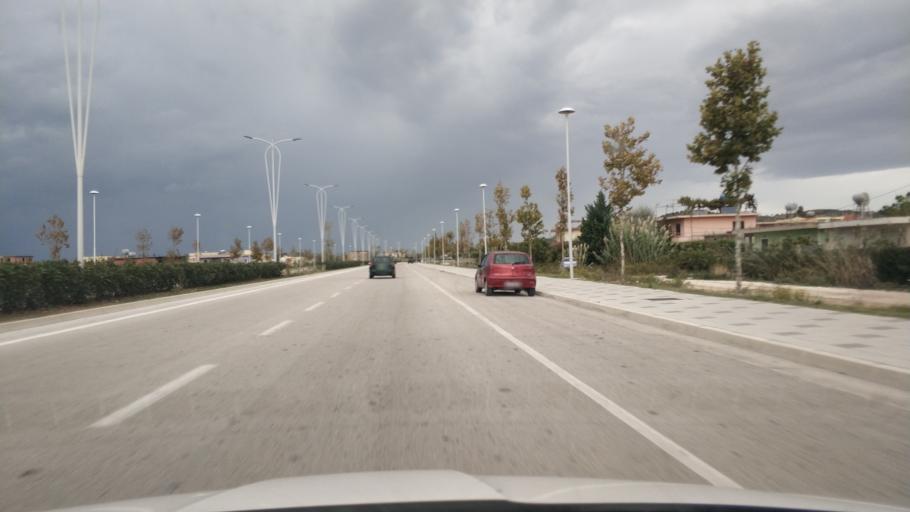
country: AL
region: Vlore
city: Vlore
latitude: 40.4810
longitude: 19.4817
